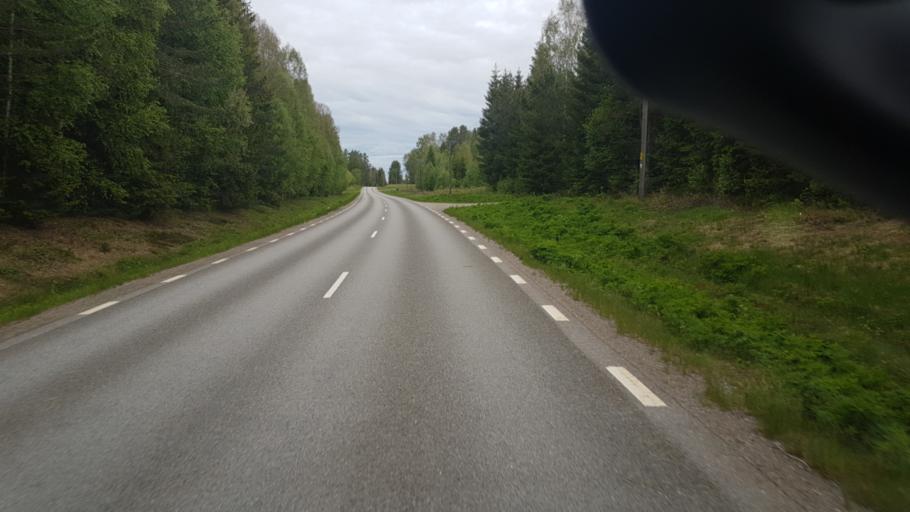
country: SE
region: Vaermland
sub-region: Arvika Kommun
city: Arvika
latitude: 59.7223
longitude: 12.5681
